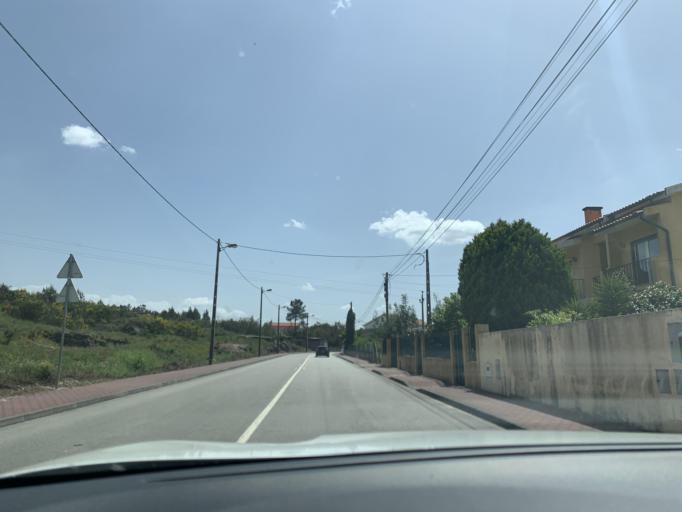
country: PT
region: Viseu
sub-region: Mangualde
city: Mangualde
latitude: 40.6102
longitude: -7.7470
